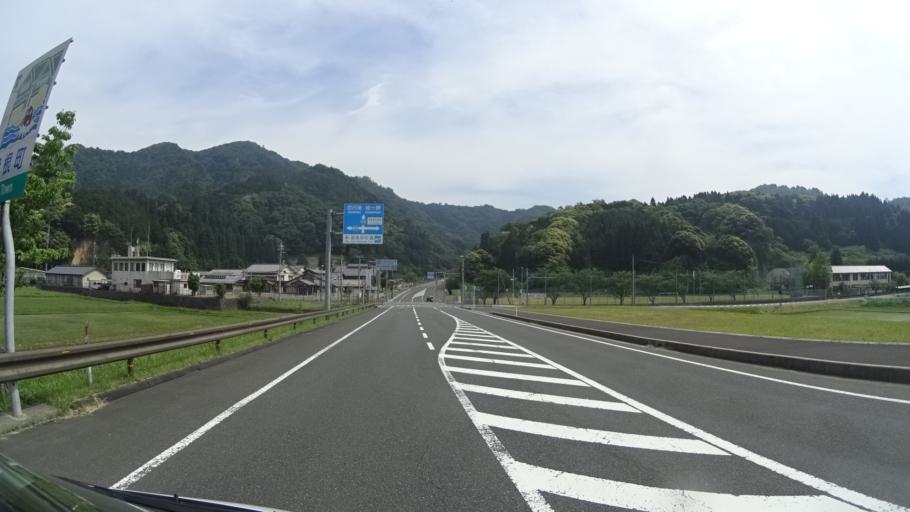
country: JP
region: Kyoto
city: Miyazu
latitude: 35.6733
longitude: 135.2722
